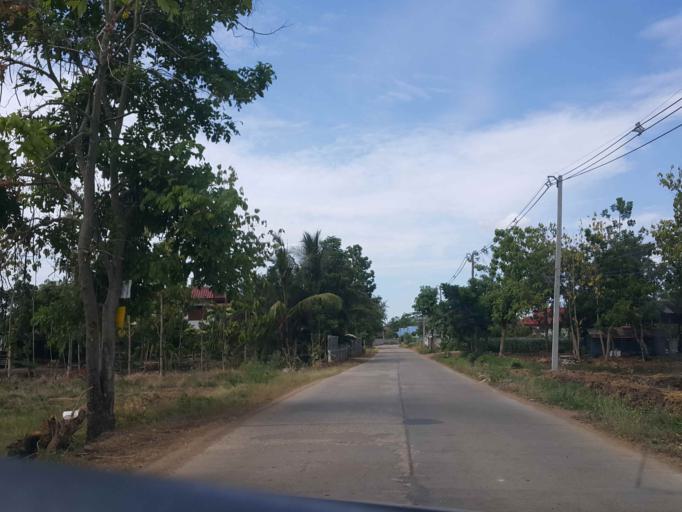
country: TH
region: Sukhothai
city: Thung Saliam
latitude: 17.3334
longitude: 99.5654
